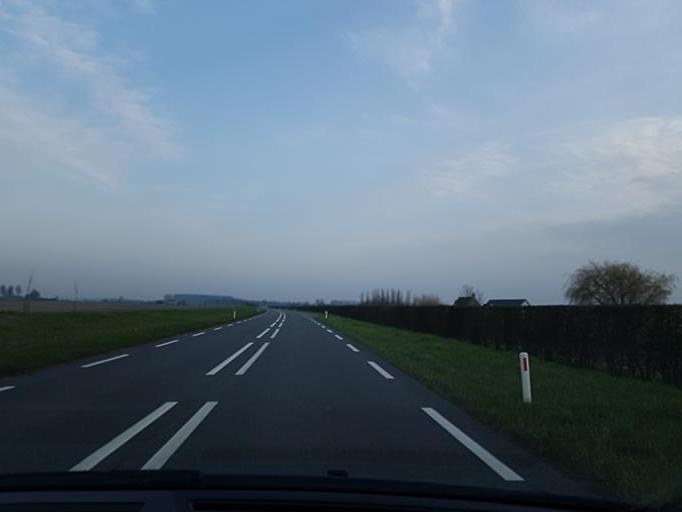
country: NL
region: Zeeland
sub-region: Gemeente Hulst
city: Hulst
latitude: 51.3553
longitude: 4.0264
